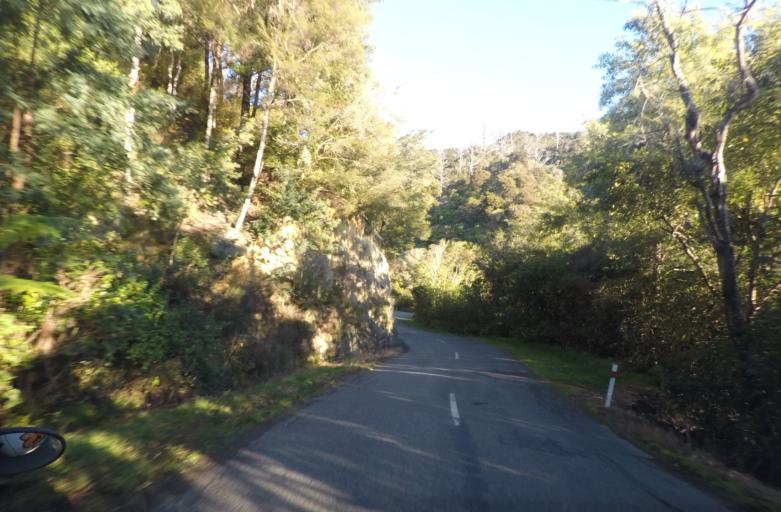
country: NZ
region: Marlborough
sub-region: Marlborough District
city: Picton
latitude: -41.2700
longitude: 173.9524
